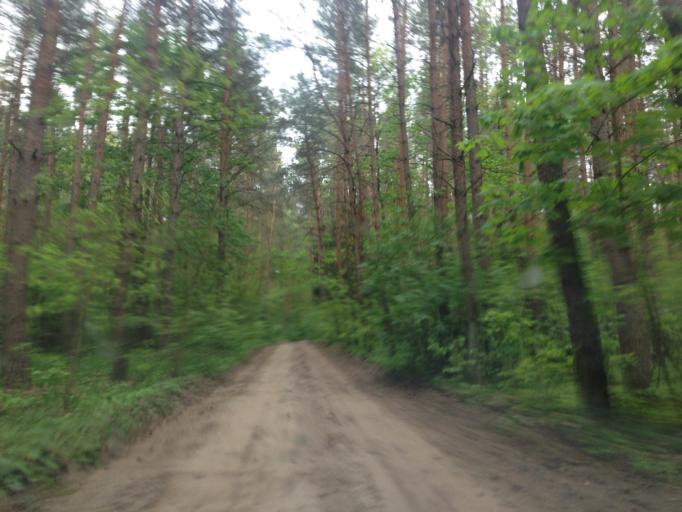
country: PL
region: Kujawsko-Pomorskie
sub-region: Powiat brodnicki
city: Bartniczka
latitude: 53.2701
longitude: 19.5321
